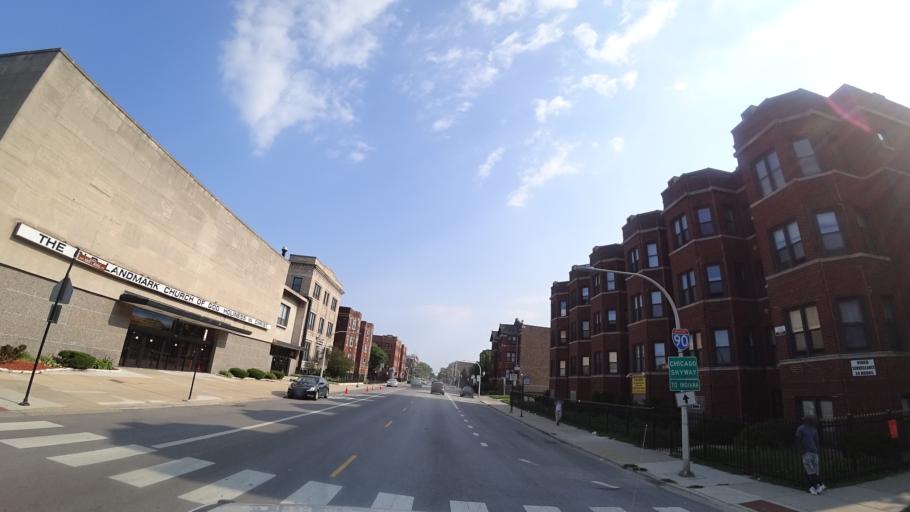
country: US
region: Illinois
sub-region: Cook County
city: Chicago
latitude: 41.7644
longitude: -87.5762
